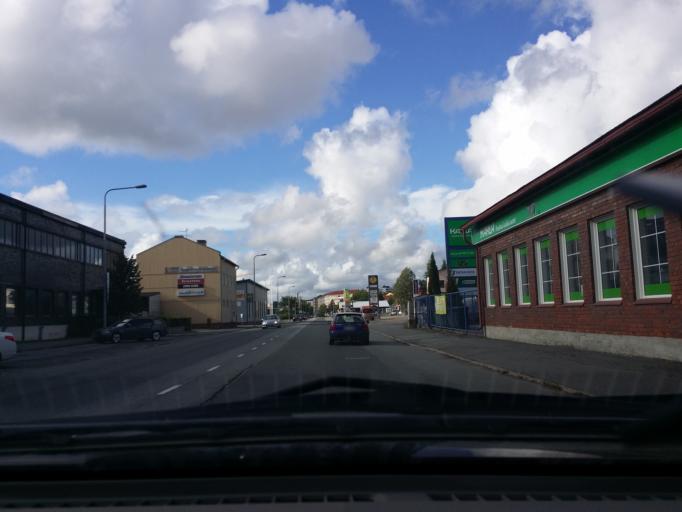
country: FI
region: Satakunta
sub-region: Pori
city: Pori
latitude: 61.4737
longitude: 21.7985
